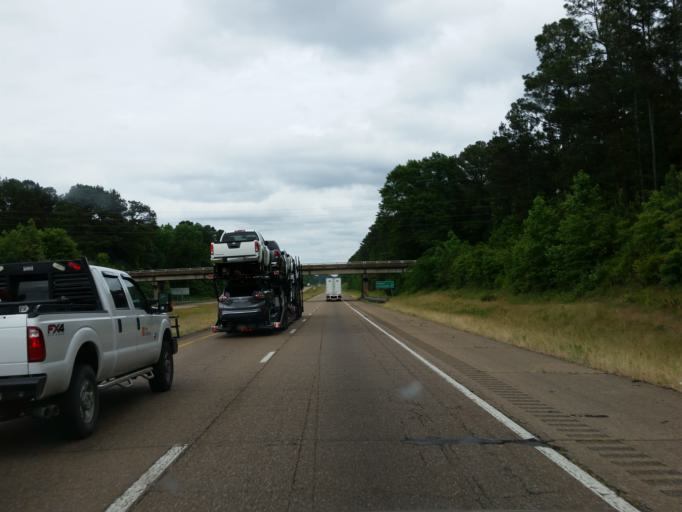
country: US
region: Mississippi
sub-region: Lauderdale County
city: Marion
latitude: 32.3856
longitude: -88.6233
